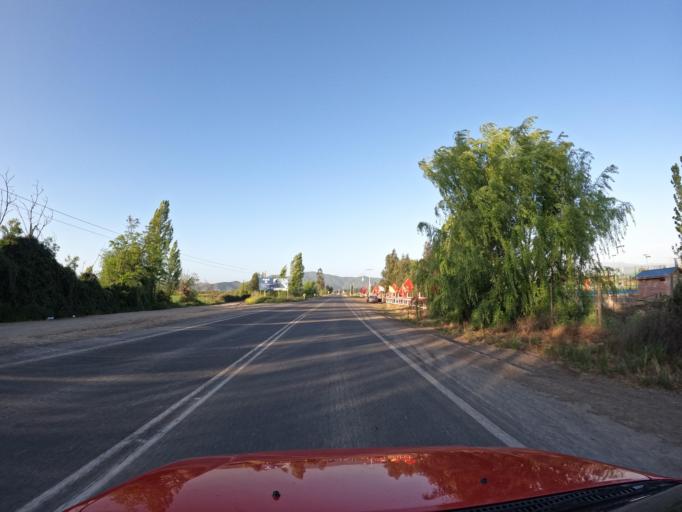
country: CL
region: O'Higgins
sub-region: Provincia de Cachapoal
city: San Vicente
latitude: -34.3018
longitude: -71.3766
